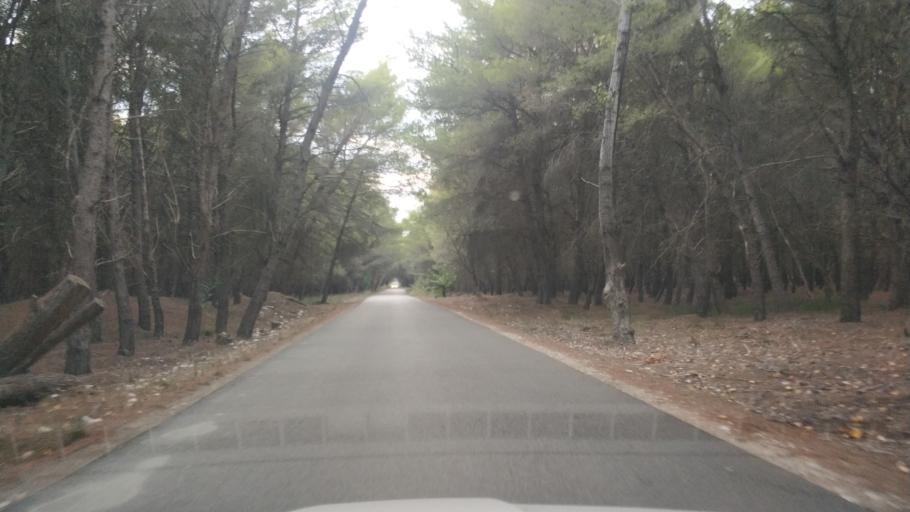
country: AL
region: Vlore
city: Vlore
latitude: 40.4966
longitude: 19.4324
